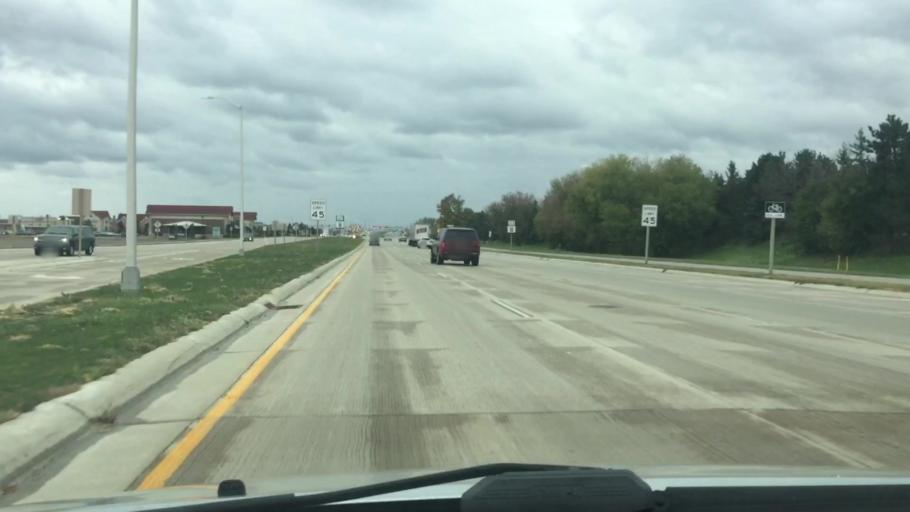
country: US
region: Wisconsin
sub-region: Waukesha County
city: Oconomowoc
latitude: 43.0810
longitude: -88.4707
